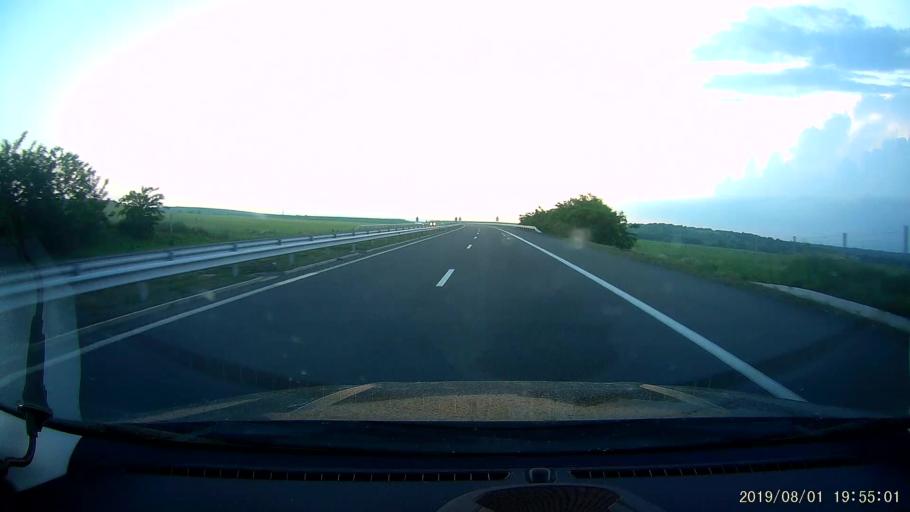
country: BG
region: Burgas
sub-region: Obshtina Karnobat
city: Karnobat
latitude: 42.5730
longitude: 26.8817
